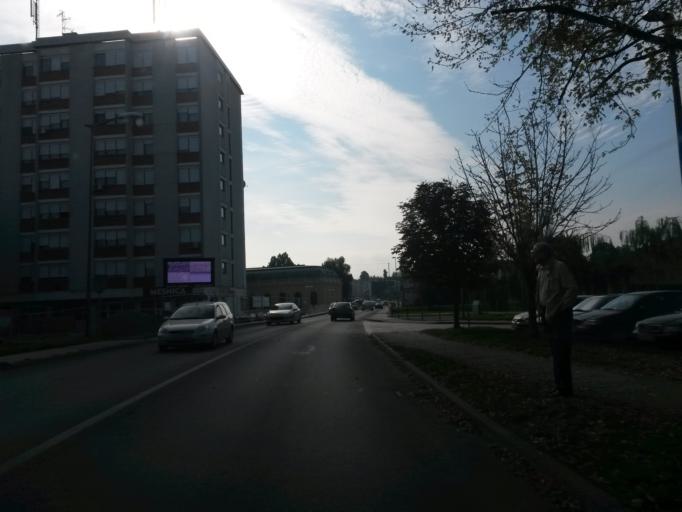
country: HR
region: Vukovarsko-Srijemska
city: Vukovar
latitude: 45.3518
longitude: 19.0008
